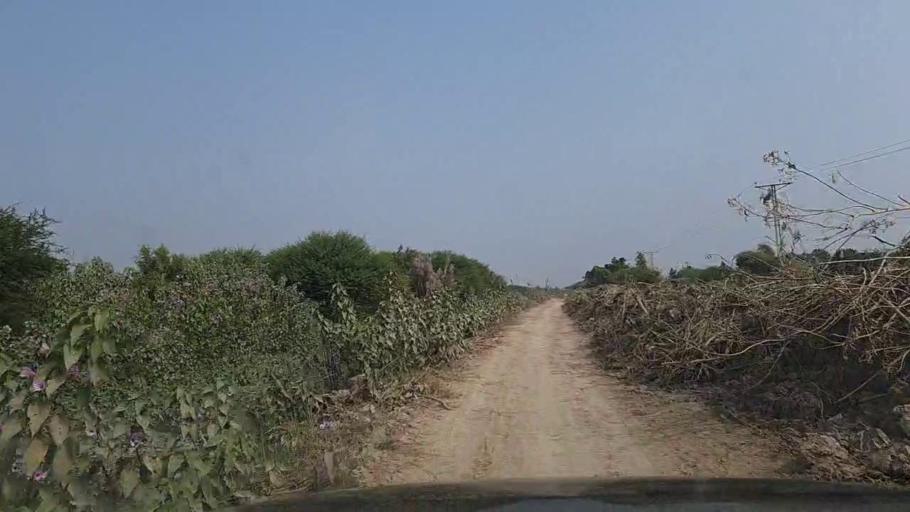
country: PK
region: Sindh
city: Thatta
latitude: 24.7570
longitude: 67.7995
